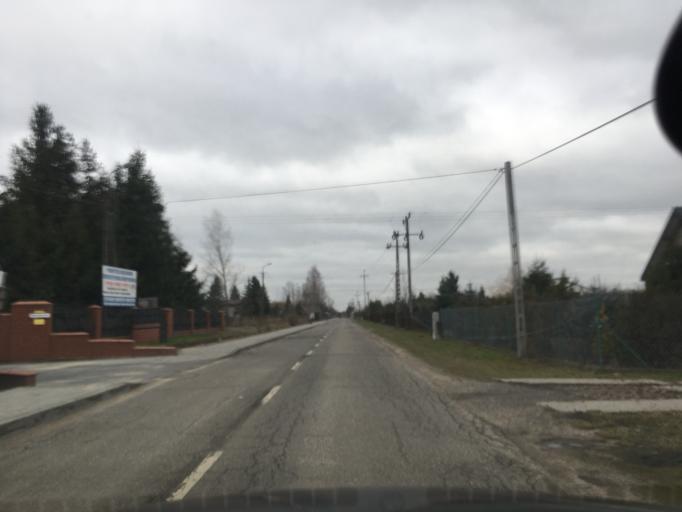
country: PL
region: Masovian Voivodeship
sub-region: Powiat piaseczynski
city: Lesznowola
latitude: 52.0429
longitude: 20.9537
